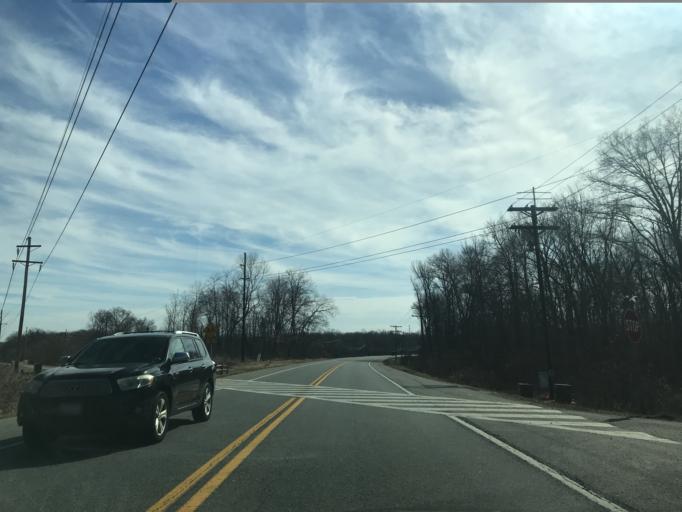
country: US
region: Maryland
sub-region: Charles County
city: Potomac Heights
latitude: 38.5947
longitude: -77.1223
